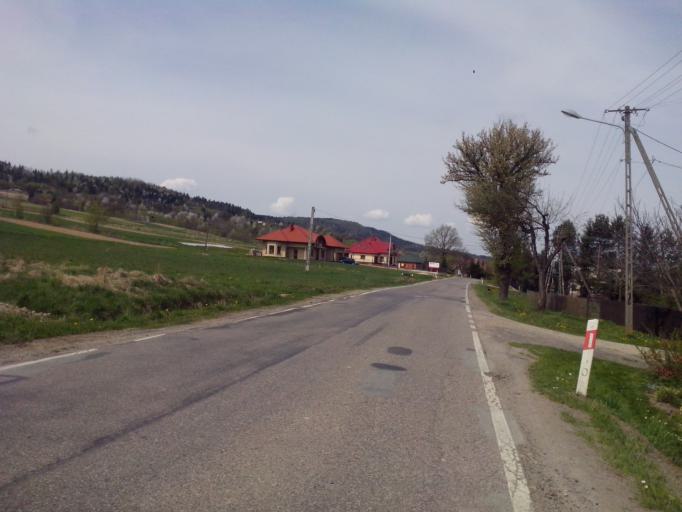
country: PL
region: Subcarpathian Voivodeship
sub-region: Powiat strzyzowski
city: Jawornik
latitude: 49.8078
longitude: 21.8536
